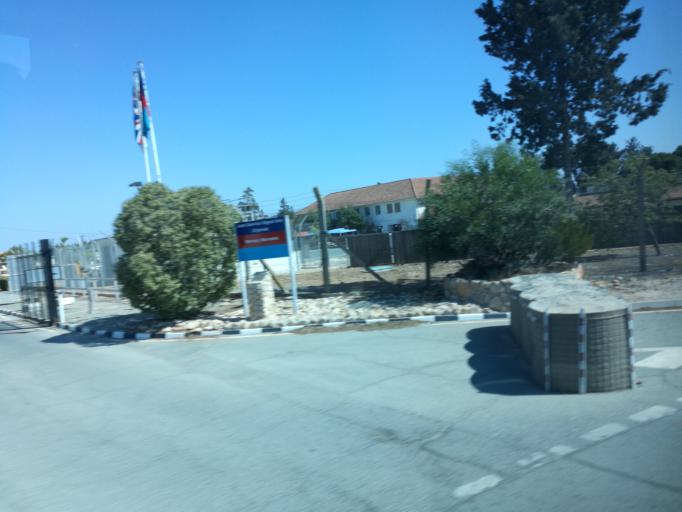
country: CY
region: Ammochostos
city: Acheritou
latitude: 35.0902
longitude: 33.8898
